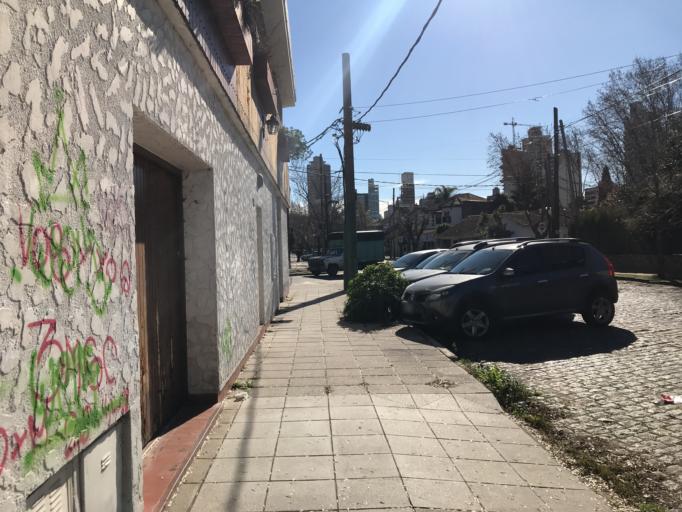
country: AR
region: Buenos Aires
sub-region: Partido de Lomas de Zamora
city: Lomas de Zamora
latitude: -34.7690
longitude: -58.4002
